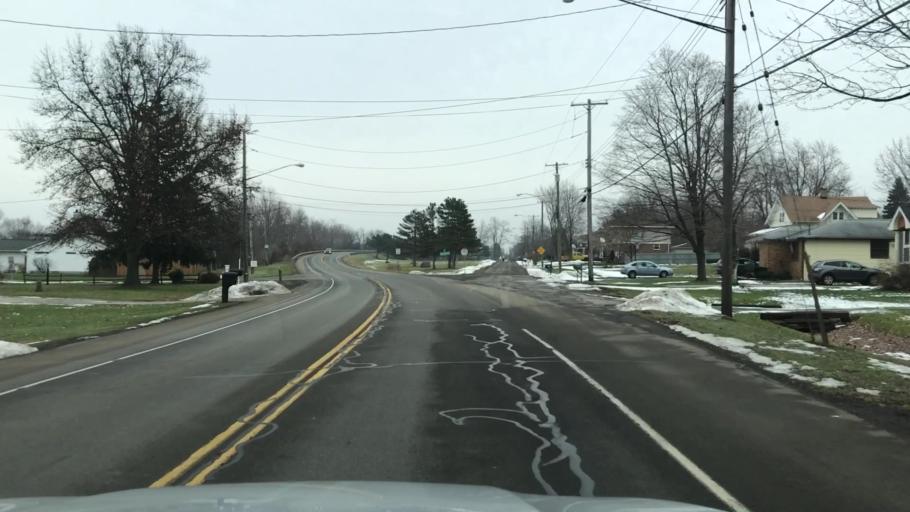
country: US
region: New York
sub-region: Erie County
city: Hamburg
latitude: 42.7514
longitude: -78.8389
